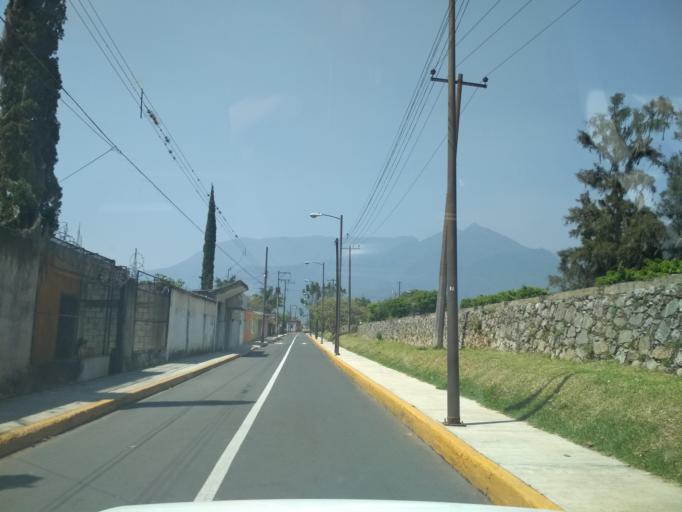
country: MX
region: Veracruz
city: Orizaba
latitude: 18.8358
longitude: -97.1097
